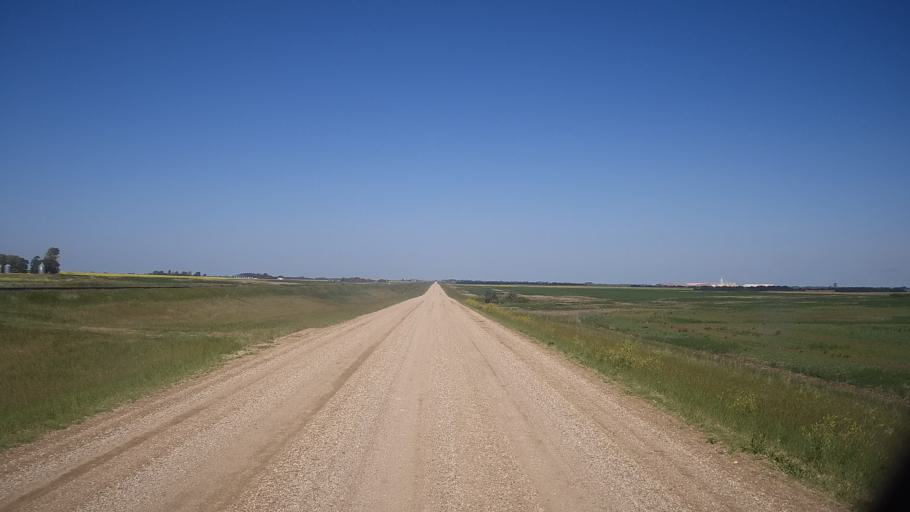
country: CA
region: Saskatchewan
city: Watrous
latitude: 51.8673
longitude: -105.9827
